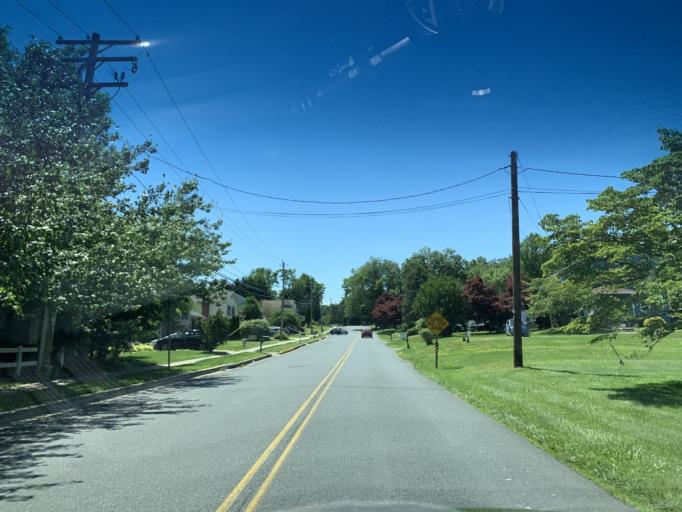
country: US
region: Maryland
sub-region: Harford County
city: Havre de Grace
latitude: 39.5538
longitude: -76.1118
